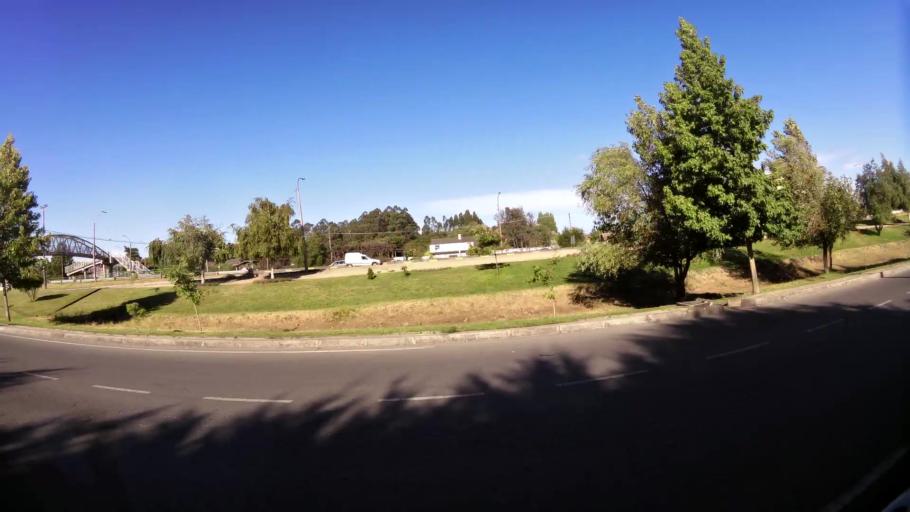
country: CL
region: Biobio
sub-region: Provincia de Concepcion
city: Concepcion
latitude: -36.8353
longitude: -73.1019
